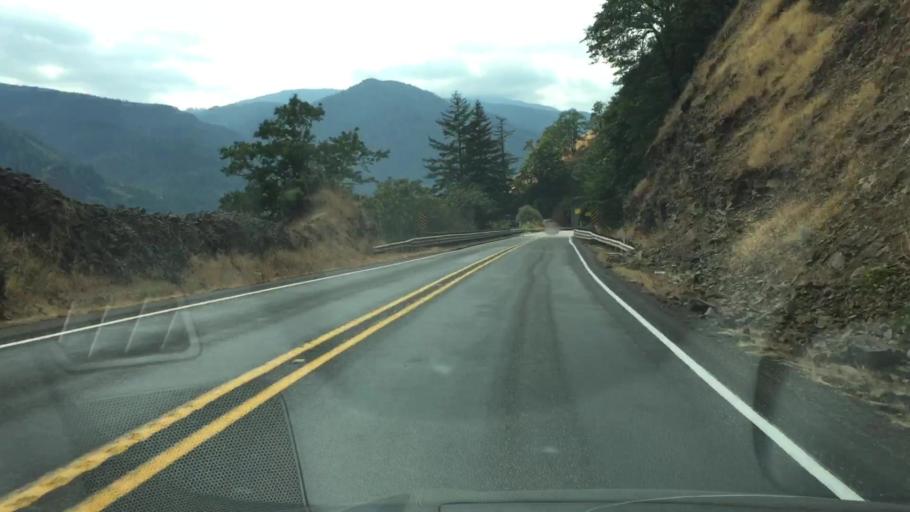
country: US
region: Oregon
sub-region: Hood River County
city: Hood River
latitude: 45.7192
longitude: -121.6075
